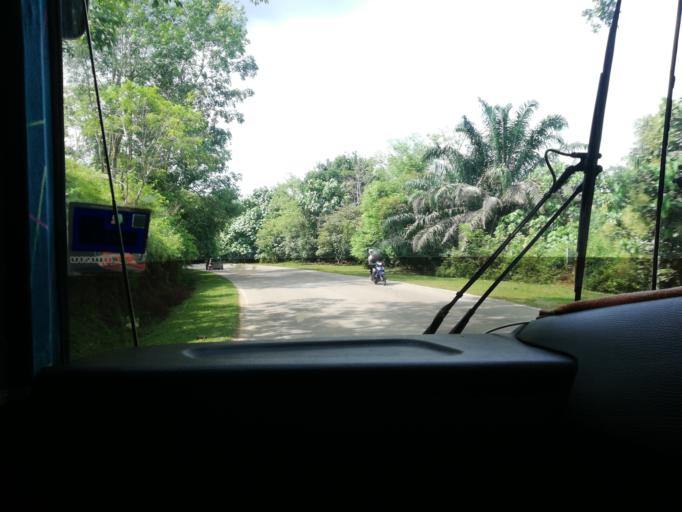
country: MY
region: Kedah
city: Kulim
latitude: 5.3263
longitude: 100.5909
